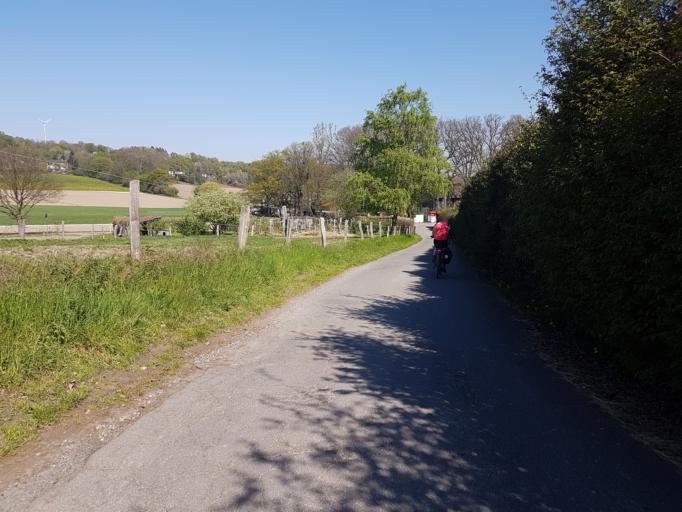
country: DE
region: North Rhine-Westphalia
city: Gevelsberg
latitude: 51.3739
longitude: 7.3294
